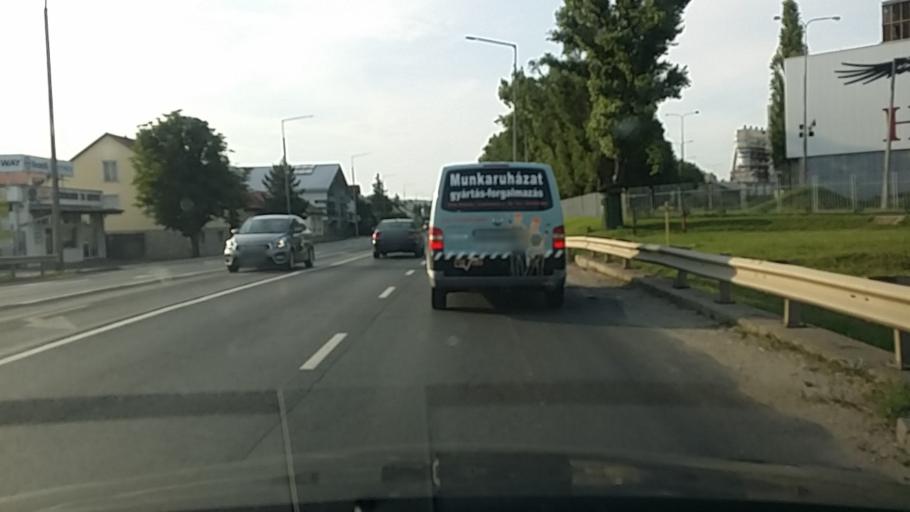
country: HU
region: Borsod-Abauj-Zemplen
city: Miskolc
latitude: 48.0615
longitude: 20.7950
